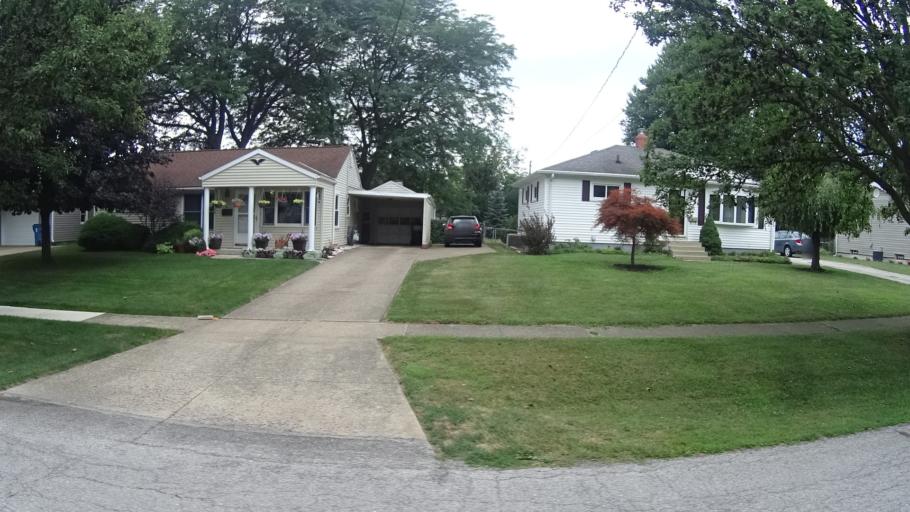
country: US
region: Ohio
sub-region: Erie County
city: Sandusky
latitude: 41.4393
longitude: -82.7640
